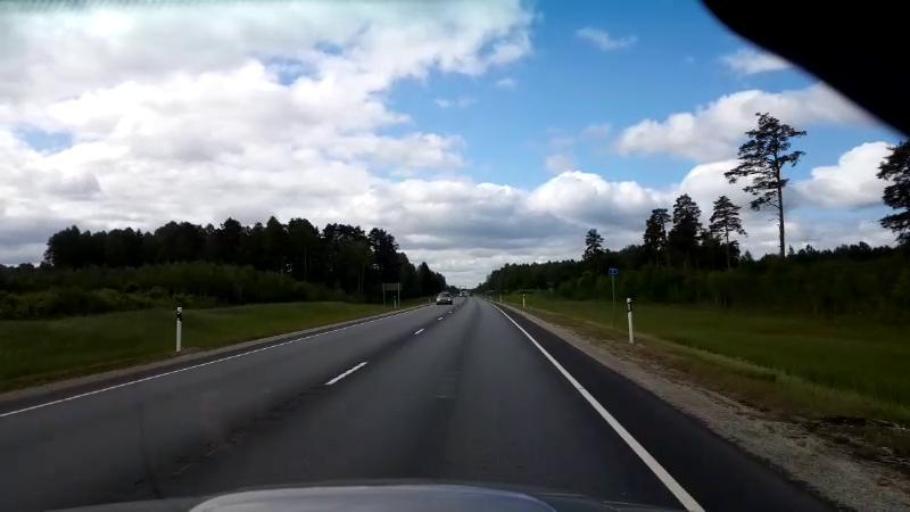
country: EE
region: Harju
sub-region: Nissi vald
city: Riisipere
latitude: 59.0724
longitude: 24.4525
